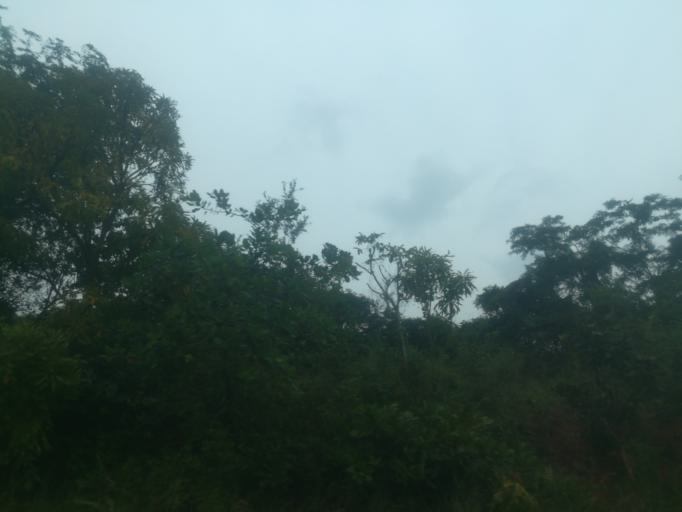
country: NG
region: Ogun
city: Ayetoro
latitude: 7.1012
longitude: 3.1328
